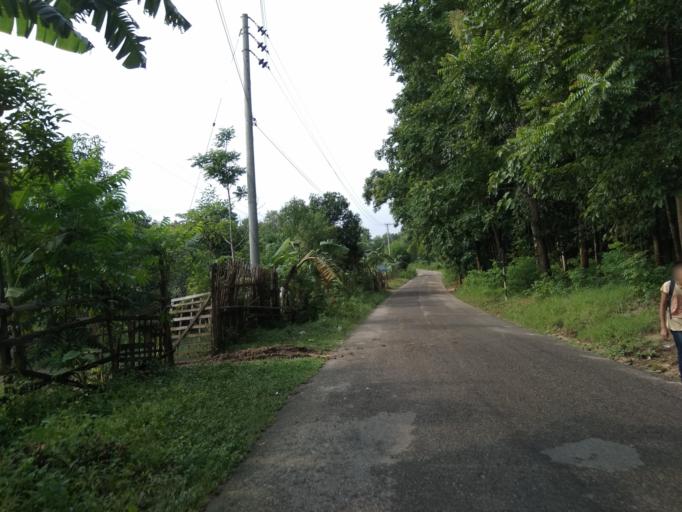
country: BD
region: Chittagong
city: Khagrachhari
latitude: 23.0287
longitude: 92.0143
